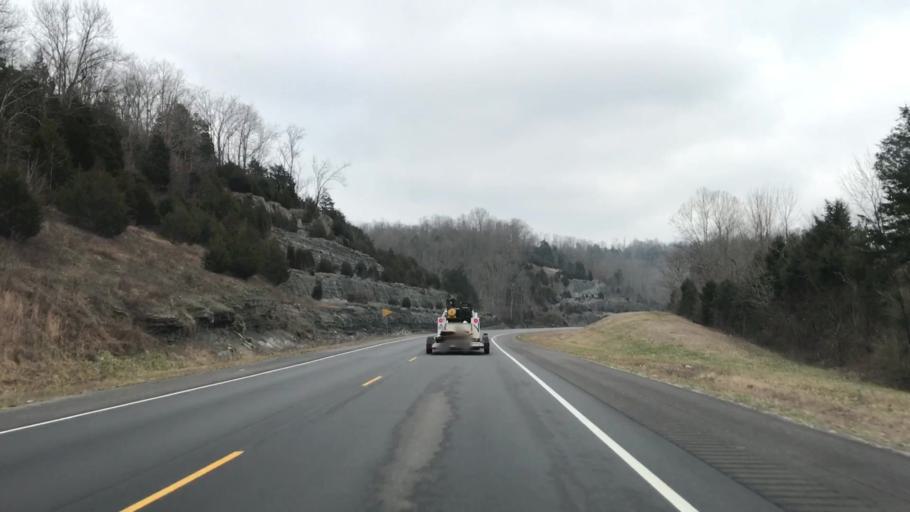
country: US
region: Kentucky
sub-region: Cumberland County
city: Burkesville
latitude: 36.9027
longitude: -85.4337
